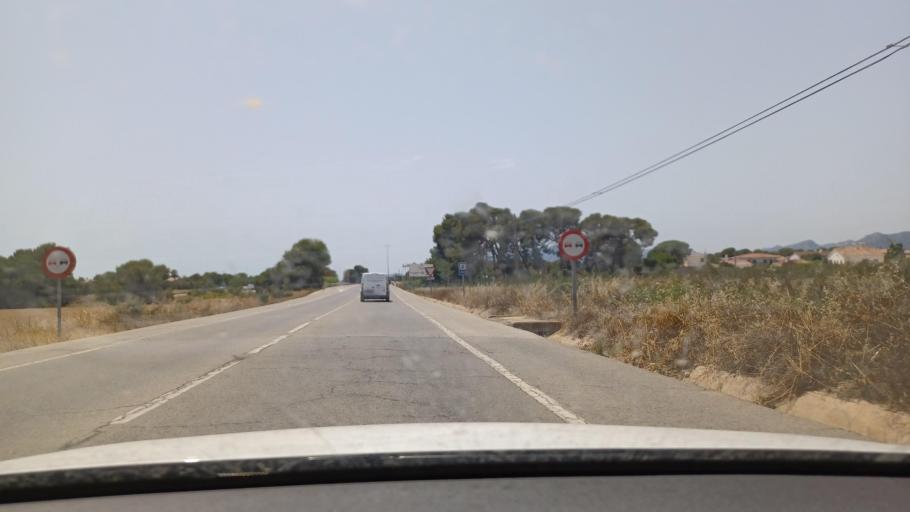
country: ES
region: Catalonia
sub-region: Provincia de Tarragona
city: Cambrils
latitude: 41.0517
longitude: 1.0024
